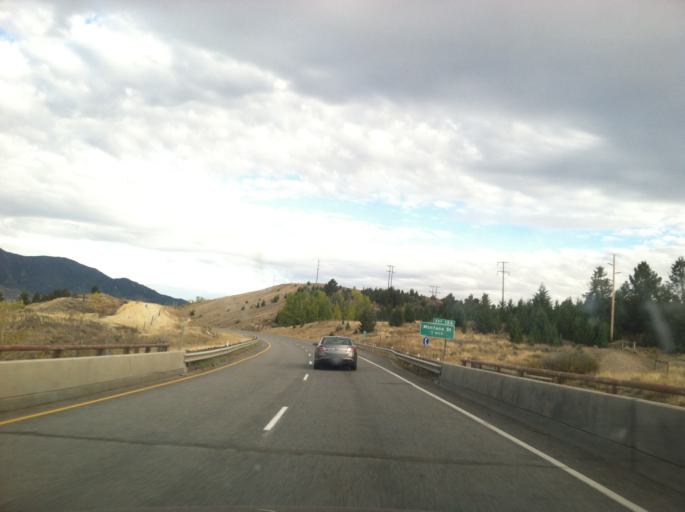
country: US
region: Montana
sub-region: Silver Bow County
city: Butte
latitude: 45.9968
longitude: -112.5664
